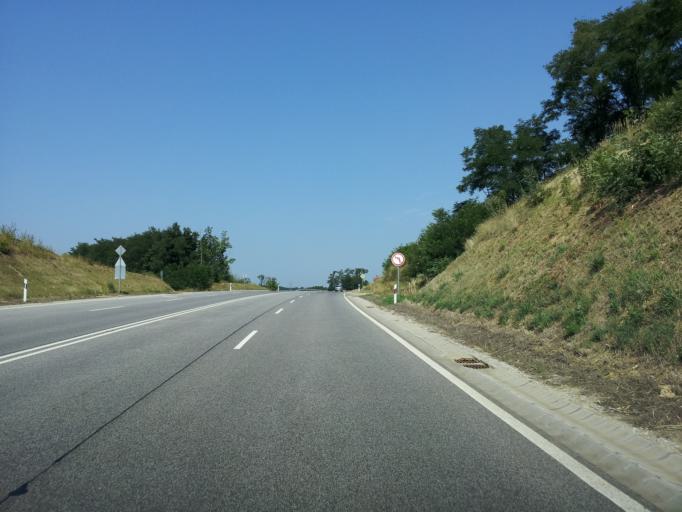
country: HU
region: Zala
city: Pacsa
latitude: 46.8298
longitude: 17.0501
